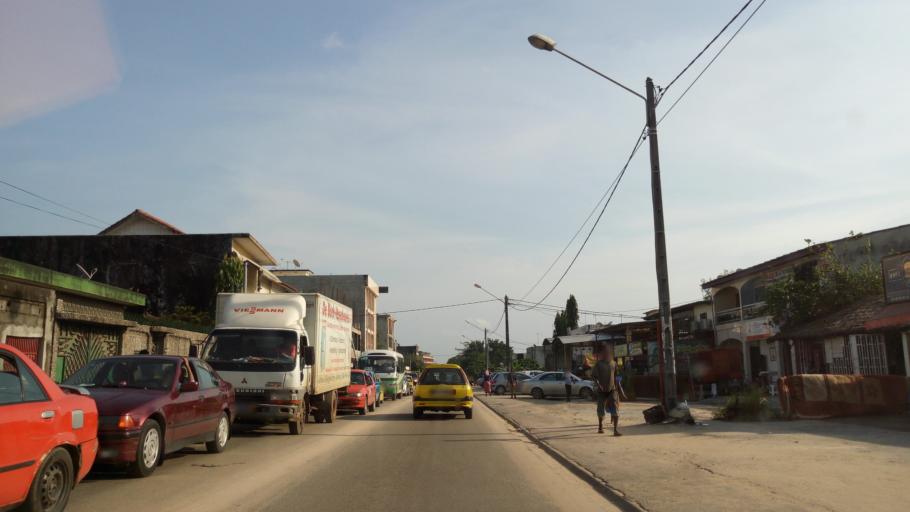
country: CI
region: Lagunes
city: Abobo
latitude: 5.3683
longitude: -3.9595
